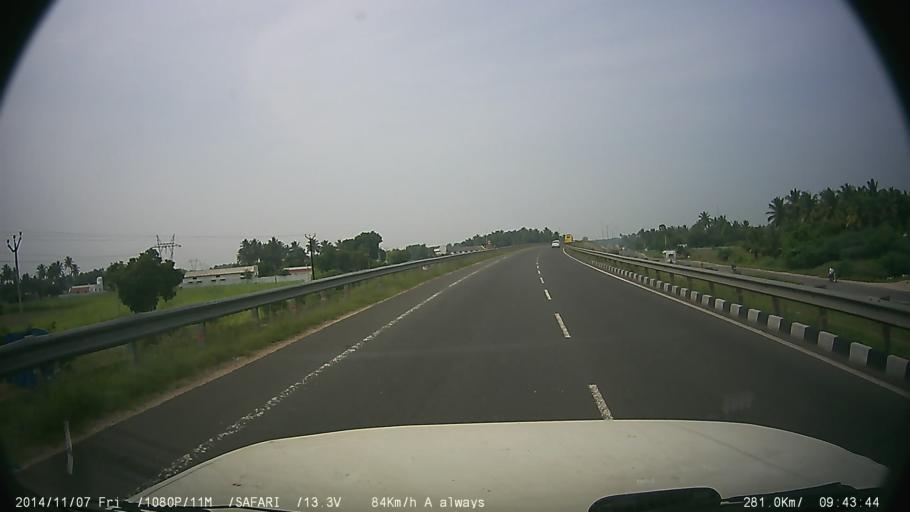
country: IN
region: Tamil Nadu
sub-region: Erode
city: Perundurai
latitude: 11.3001
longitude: 77.5992
